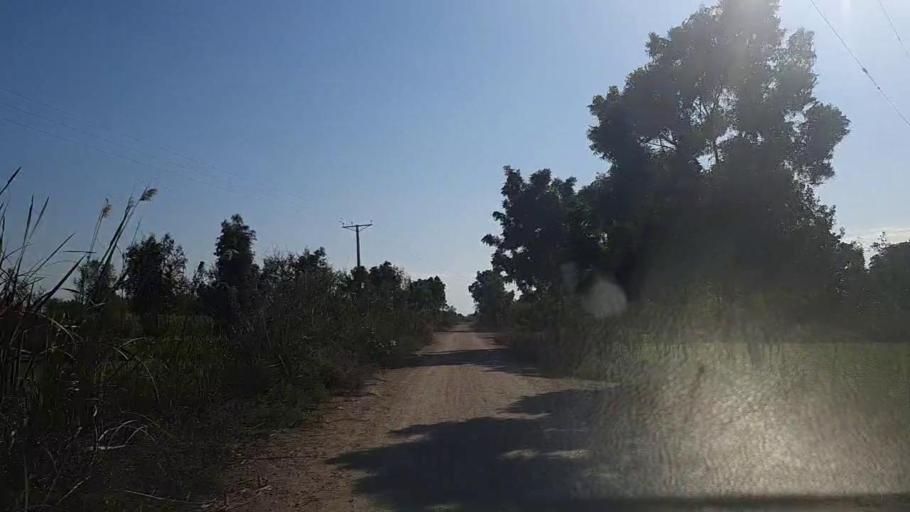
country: PK
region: Sindh
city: Khadro
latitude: 26.2727
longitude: 68.8158
